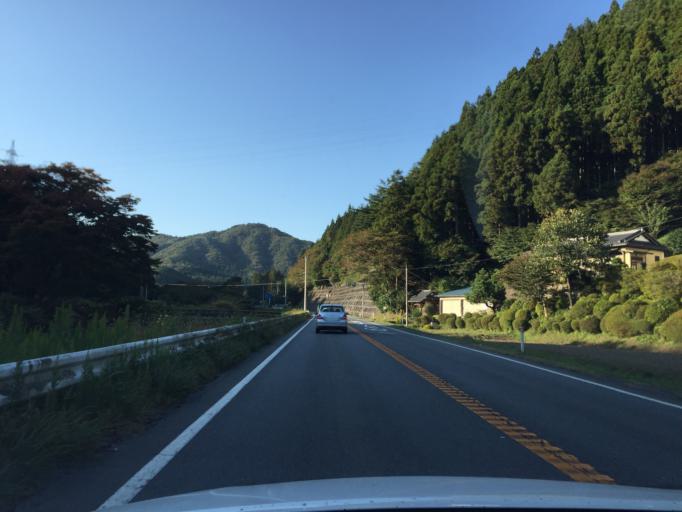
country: JP
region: Fukushima
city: Iwaki
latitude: 37.0798
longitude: 140.7833
